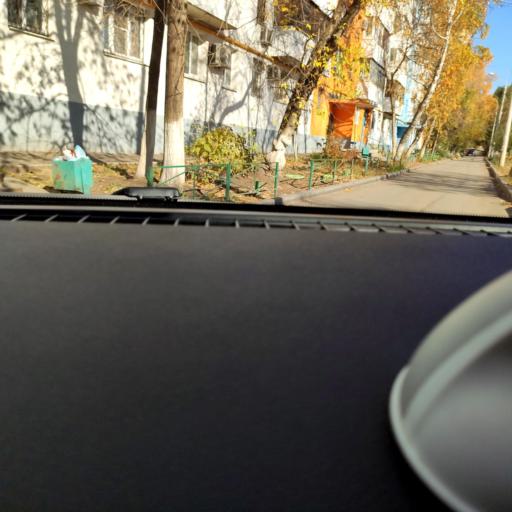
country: RU
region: Samara
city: Samara
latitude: 53.2513
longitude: 50.2270
